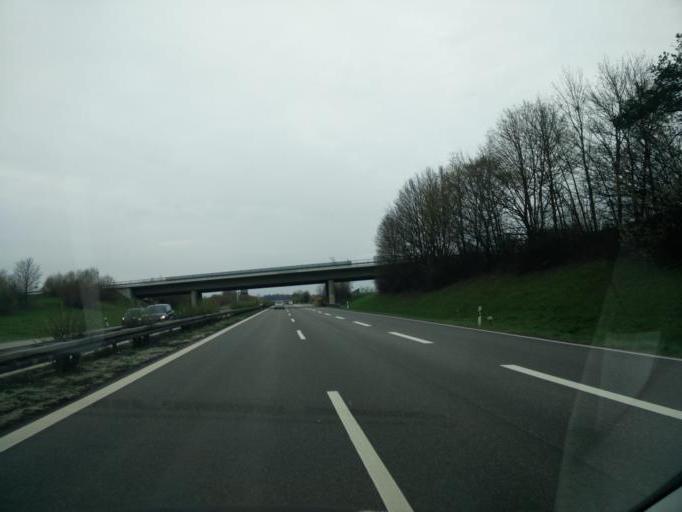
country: DE
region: Baden-Wuerttemberg
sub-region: Tuebingen Region
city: Pliezhausen
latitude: 48.5787
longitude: 9.1745
